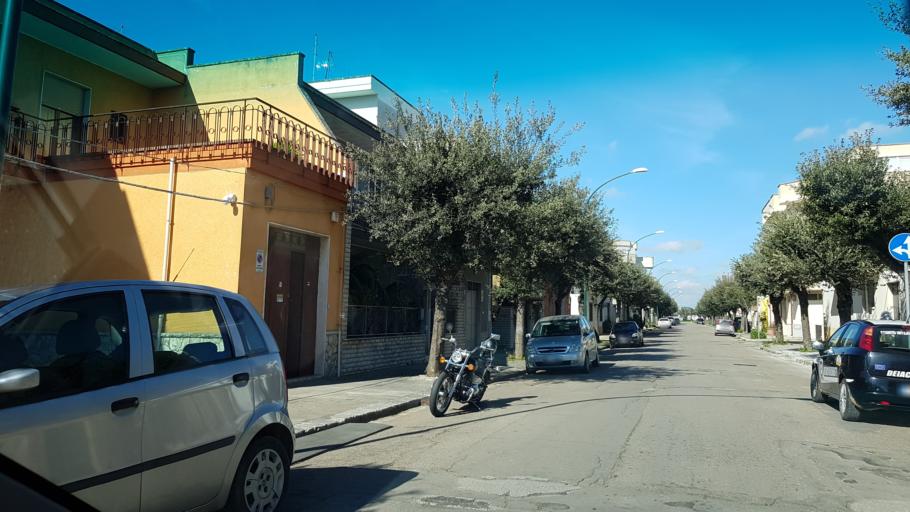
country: IT
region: Apulia
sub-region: Provincia di Lecce
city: Campi Salentina
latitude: 40.3968
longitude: 18.0112
